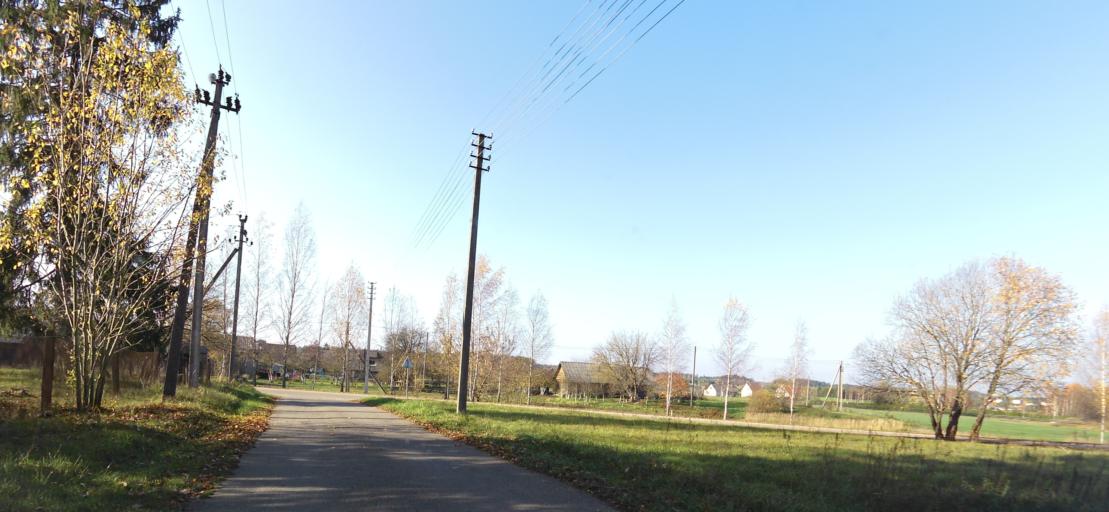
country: LT
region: Vilnius County
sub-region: Trakai
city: Rudiskes
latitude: 54.4953
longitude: 24.6787
